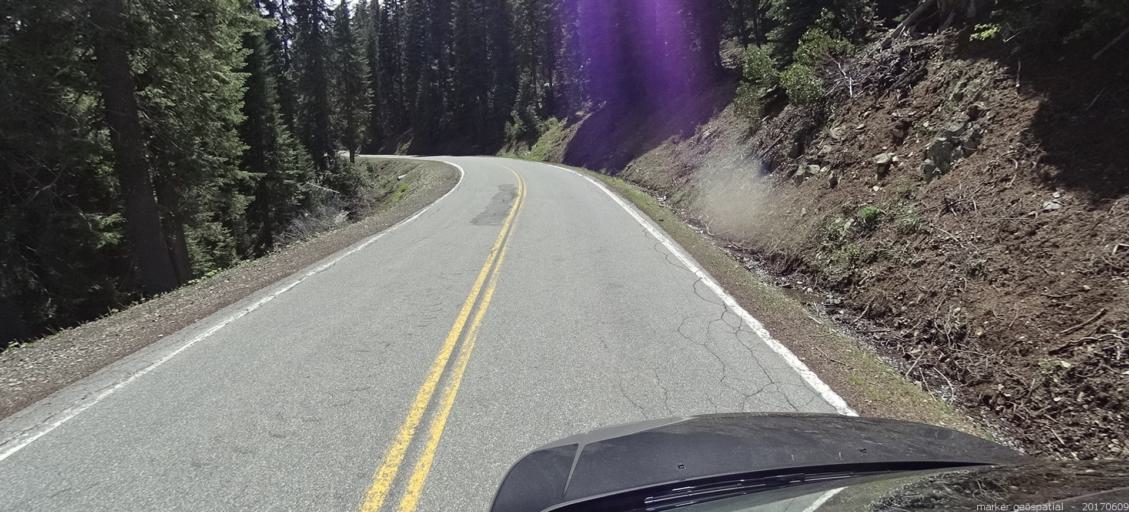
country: US
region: California
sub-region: Siskiyou County
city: Yreka
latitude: 41.4010
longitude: -122.9966
